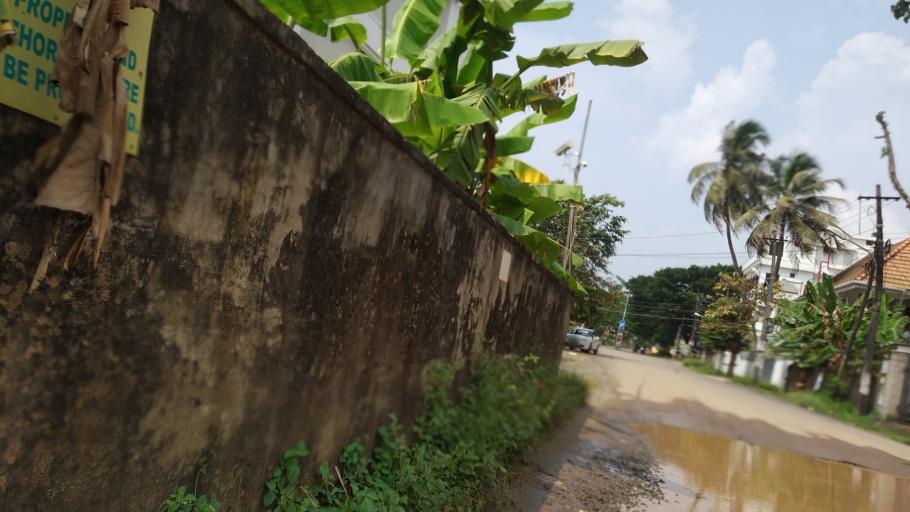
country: IN
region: Kerala
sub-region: Ernakulam
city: Cochin
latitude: 9.9708
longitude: 76.3019
